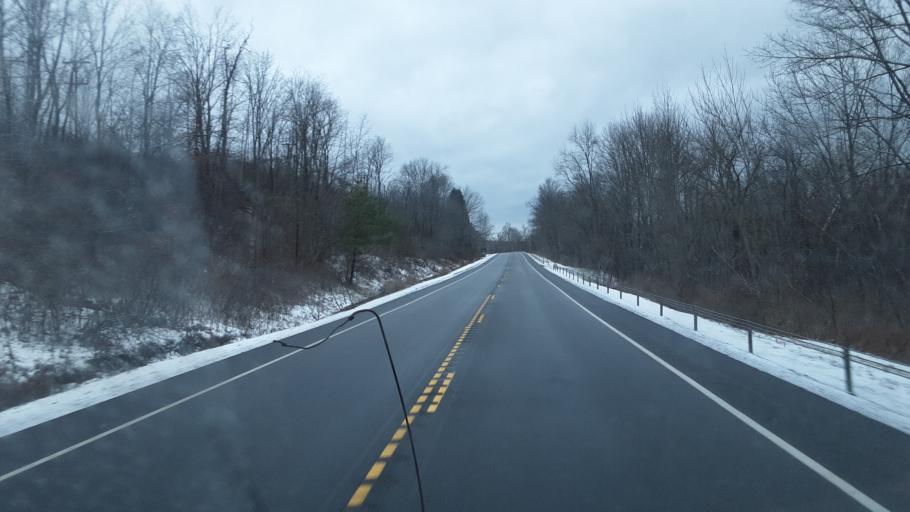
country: US
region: New York
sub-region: Allegany County
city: Belmont
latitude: 42.2910
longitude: -78.0695
